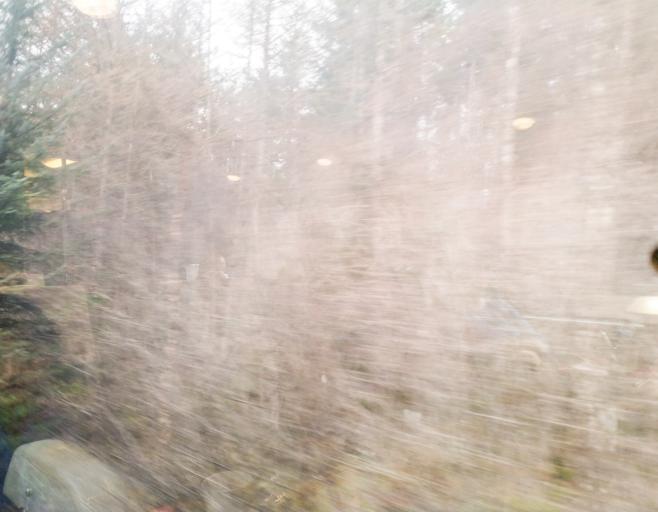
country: GB
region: Scotland
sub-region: Highland
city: Spean Bridge
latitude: 56.8920
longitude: -4.9074
